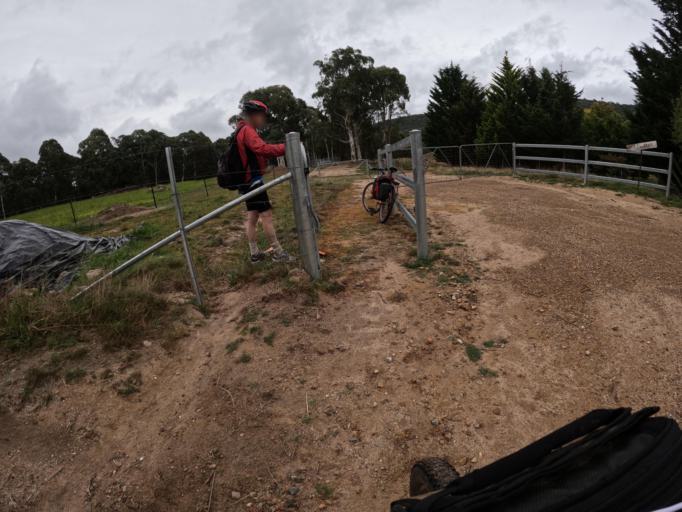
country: AU
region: New South Wales
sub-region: Greater Hume Shire
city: Holbrook
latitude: -36.1454
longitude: 147.4516
